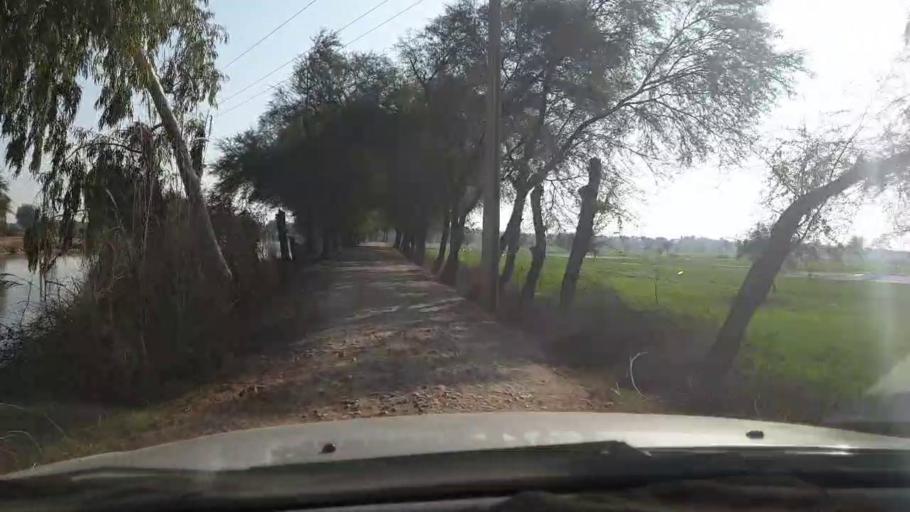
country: PK
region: Sindh
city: Mirpur Mathelo
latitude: 27.9901
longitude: 69.5447
